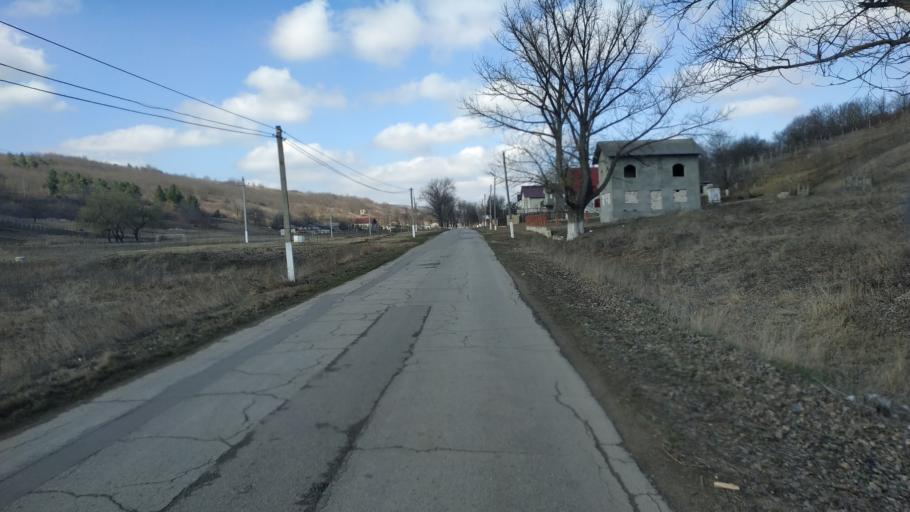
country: MD
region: Hincesti
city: Hincesti
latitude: 46.8716
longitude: 28.6351
